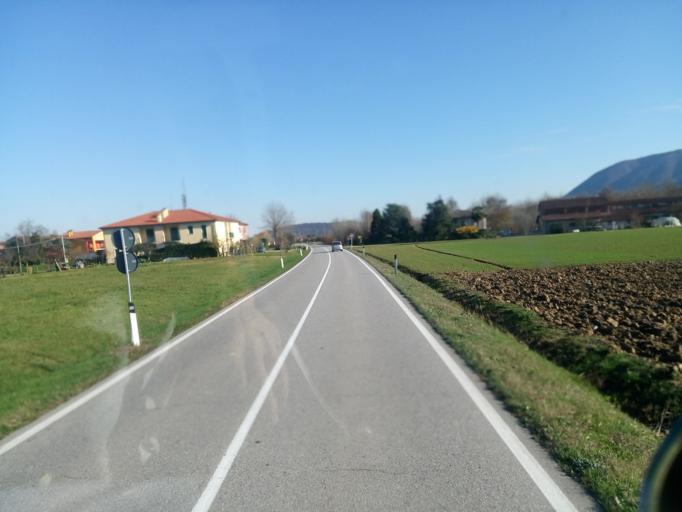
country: IT
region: Veneto
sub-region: Provincia di Padova
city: Bastia
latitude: 45.3795
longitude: 11.6159
